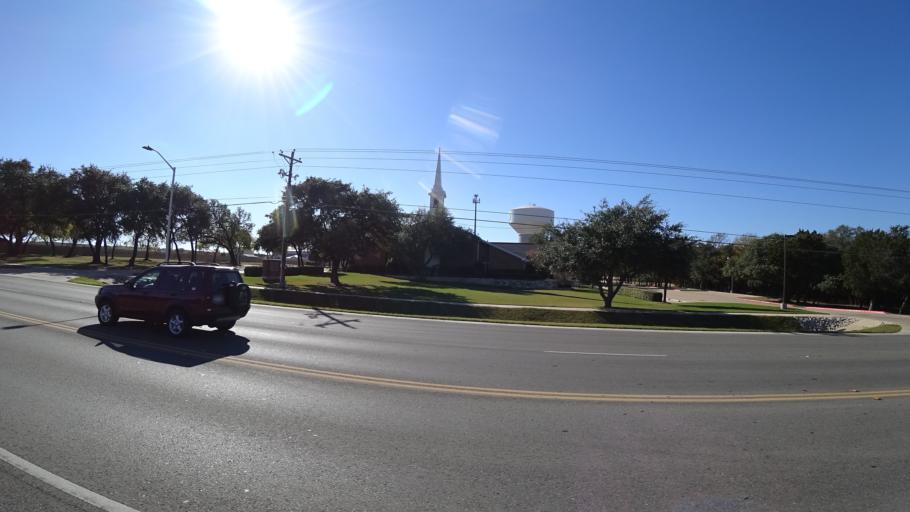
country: US
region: Texas
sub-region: Williamson County
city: Cedar Park
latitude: 30.5325
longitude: -97.8460
